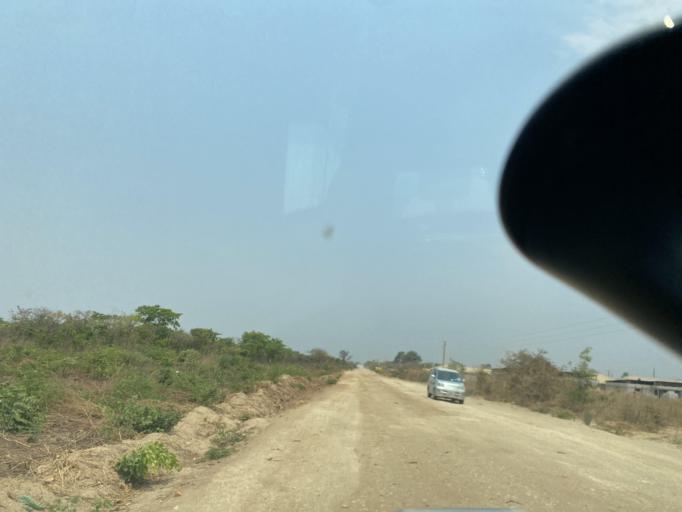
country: ZM
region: Lusaka
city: Lusaka
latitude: -15.5210
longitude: 28.3421
